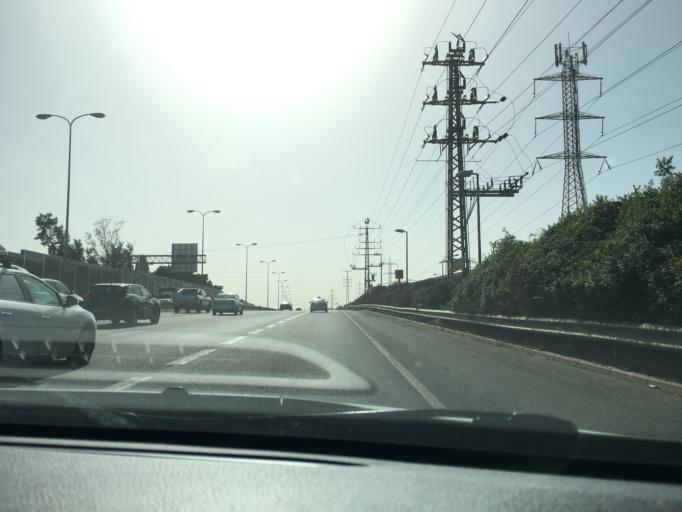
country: IL
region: Central District
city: Hod HaSharon
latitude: 32.1668
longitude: 34.8808
